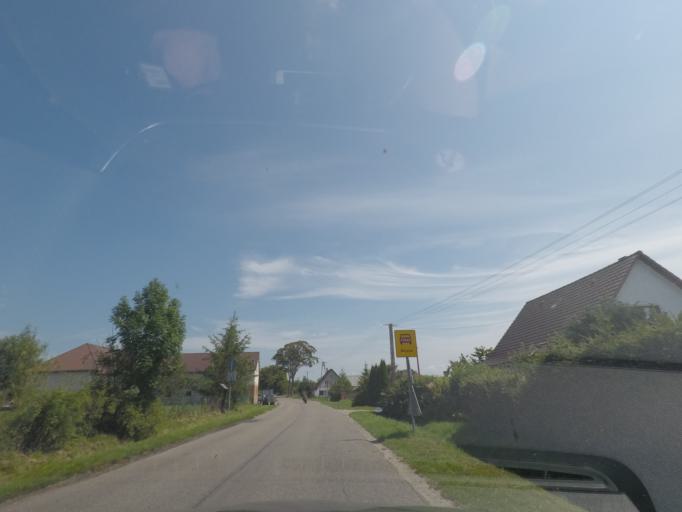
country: PL
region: West Pomeranian Voivodeship
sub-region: Powiat slawienski
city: Darlowo
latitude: 54.4623
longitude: 16.5255
